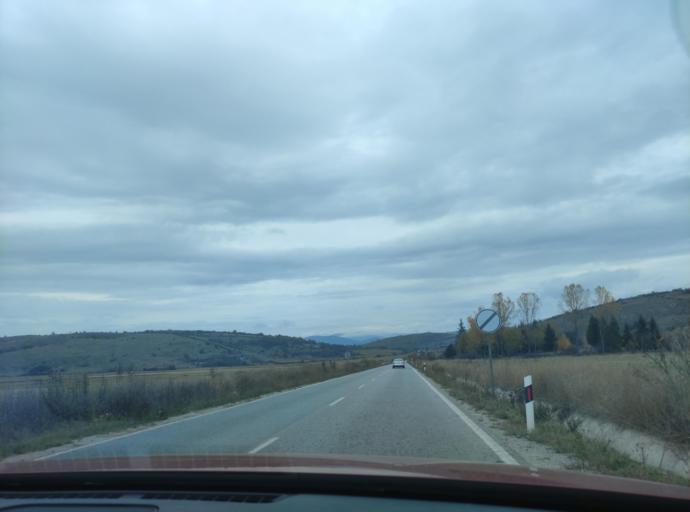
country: BG
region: Sofiya
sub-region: Obshtina Godech
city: Godech
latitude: 42.9497
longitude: 23.1589
